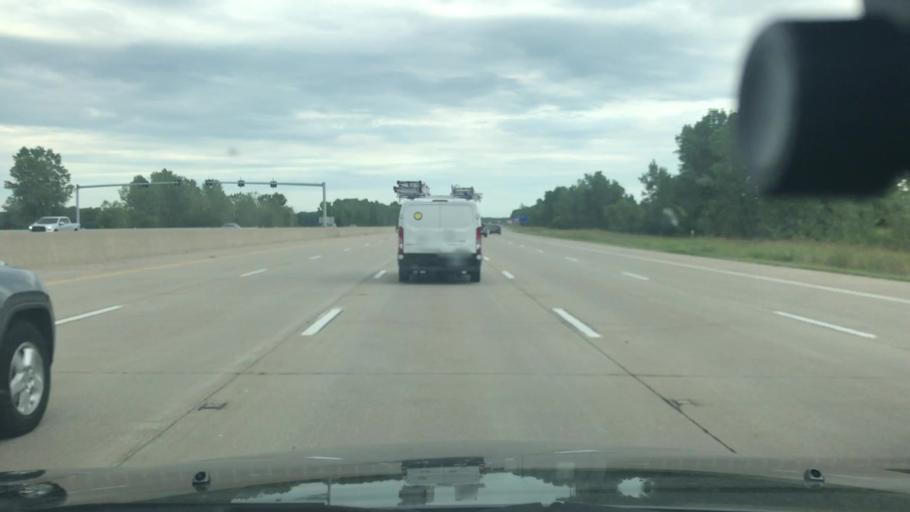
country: US
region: Missouri
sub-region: Saint Charles County
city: Saint Charles
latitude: 38.7270
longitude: -90.5150
